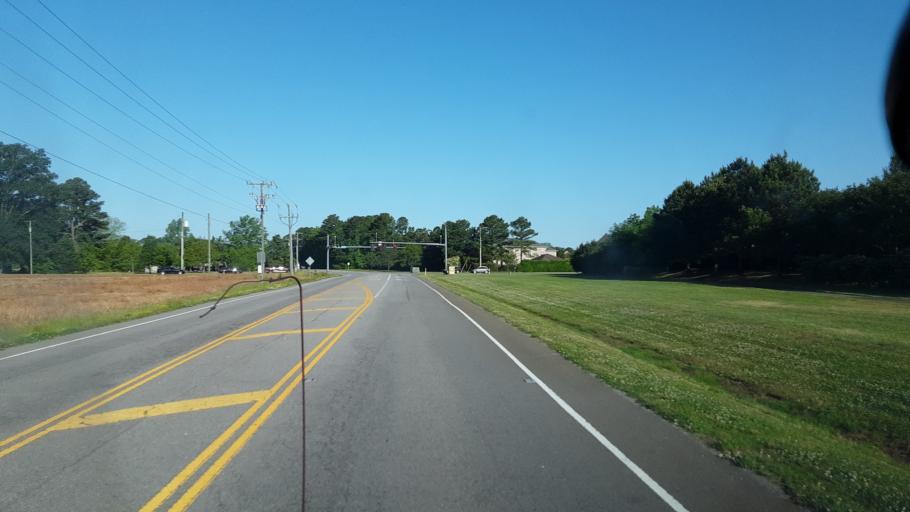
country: US
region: Virginia
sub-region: City of Virginia Beach
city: Virginia Beach
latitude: 36.7217
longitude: -76.0498
